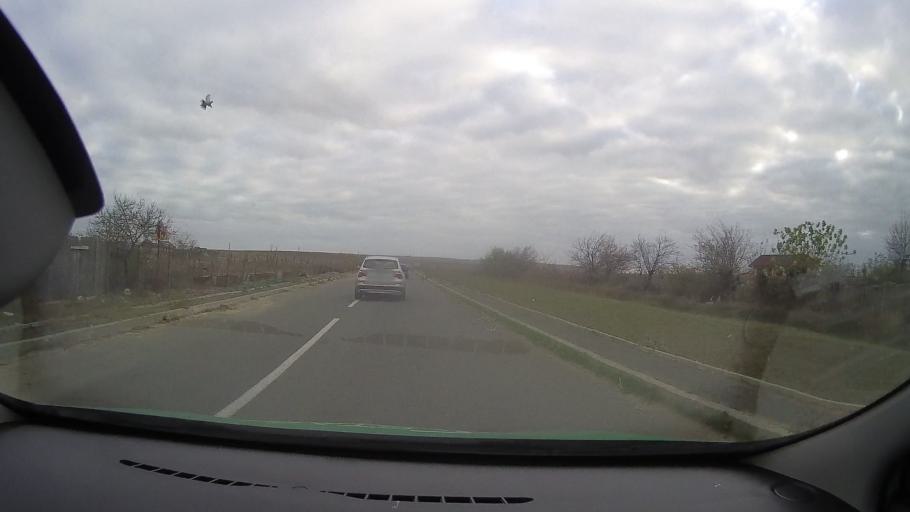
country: RO
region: Tulcea
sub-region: Comuna Jurilovca
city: Jurilovca
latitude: 44.7603
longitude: 28.8847
